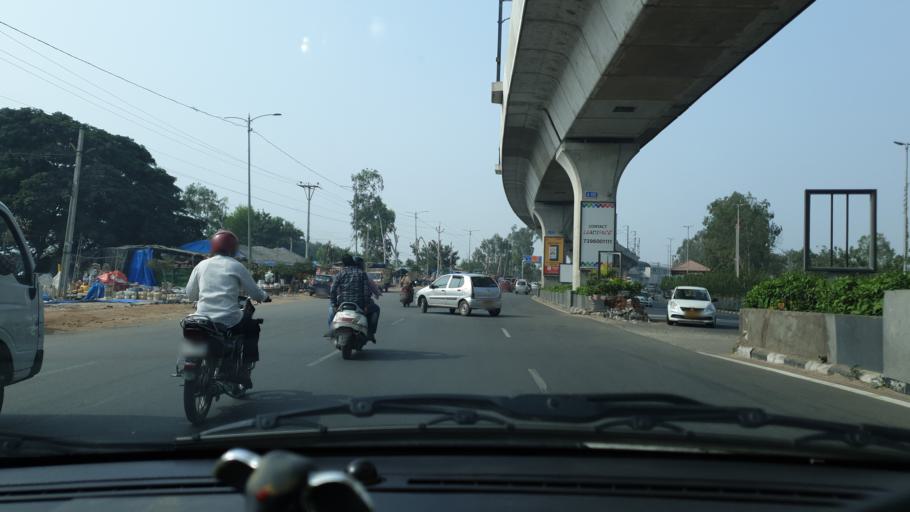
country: IN
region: Telangana
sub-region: Rangareddi
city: Kukatpalli
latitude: 17.4977
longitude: 78.3759
